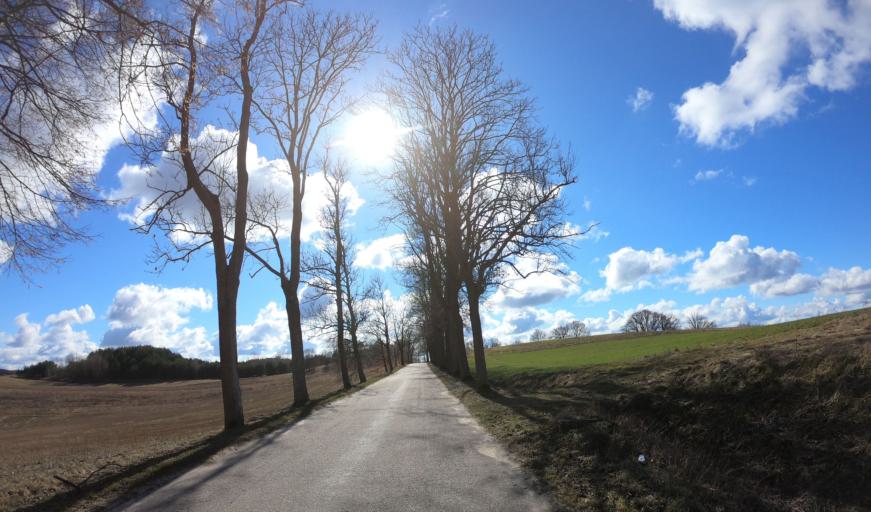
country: PL
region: West Pomeranian Voivodeship
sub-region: Powiat drawski
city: Zlocieniec
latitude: 53.4718
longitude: 15.9694
